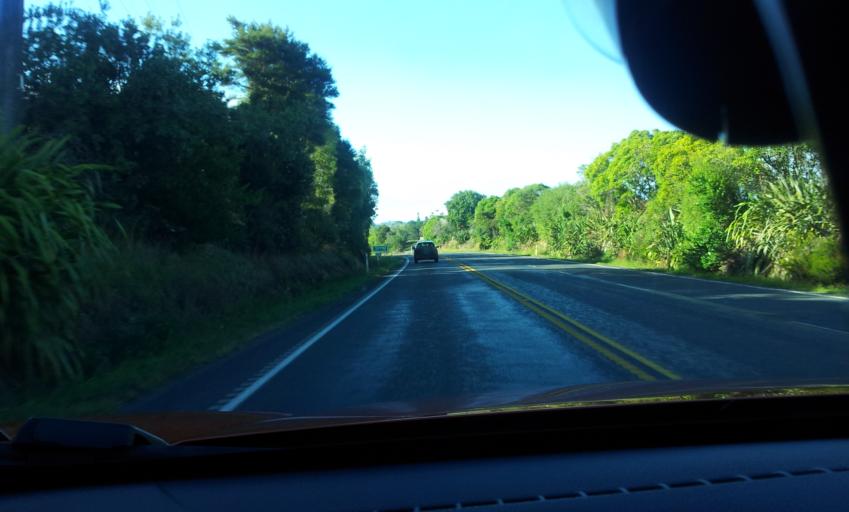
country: NZ
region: Waikato
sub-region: Hauraki District
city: Ngatea
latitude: -37.2881
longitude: 175.3701
